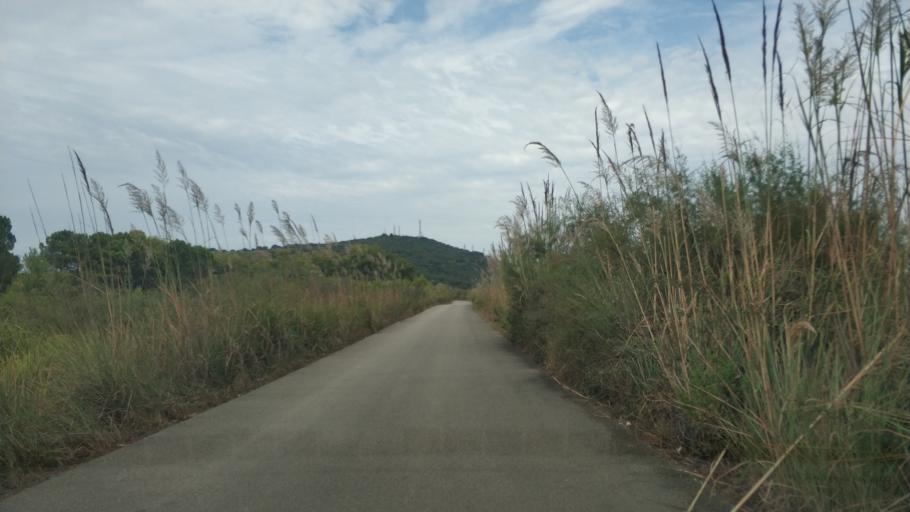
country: AL
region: Vlore
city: Vlore
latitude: 40.5031
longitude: 19.4265
